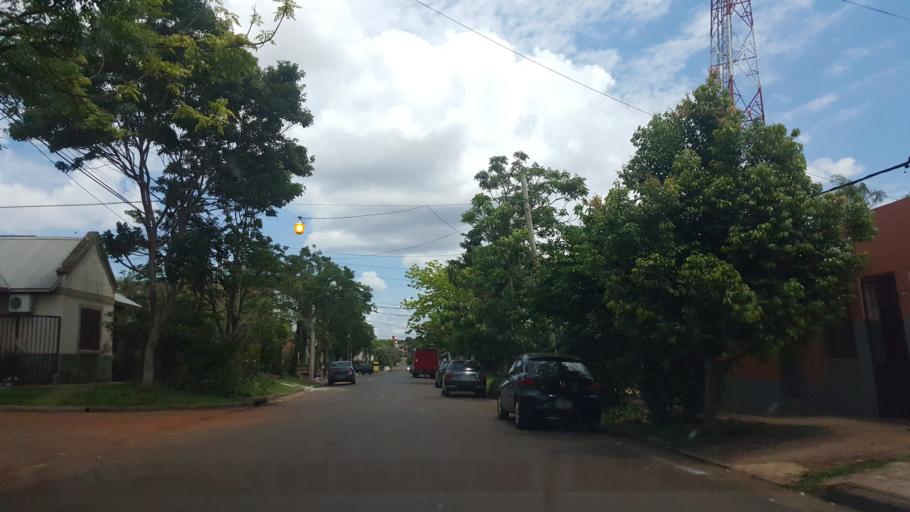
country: AR
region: Misiones
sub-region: Departamento de Capital
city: Posadas
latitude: -27.3786
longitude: -55.9083
